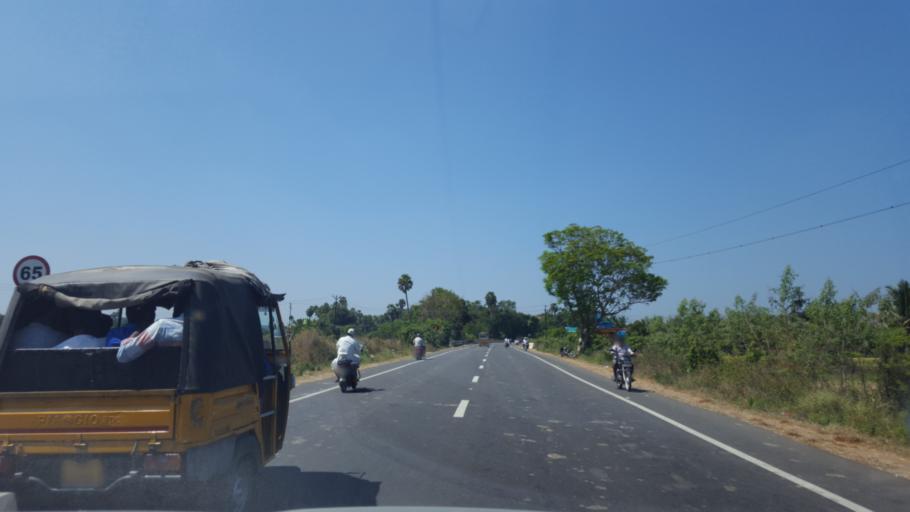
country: IN
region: Tamil Nadu
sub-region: Kancheepuram
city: Karumbakkam
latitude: 12.6396
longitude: 80.0435
